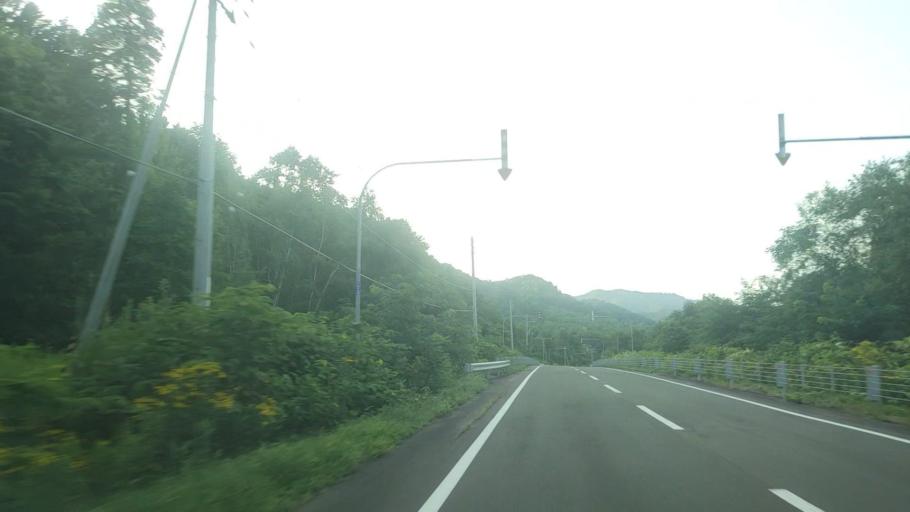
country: JP
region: Hokkaido
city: Bibai
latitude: 43.0799
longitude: 142.1006
